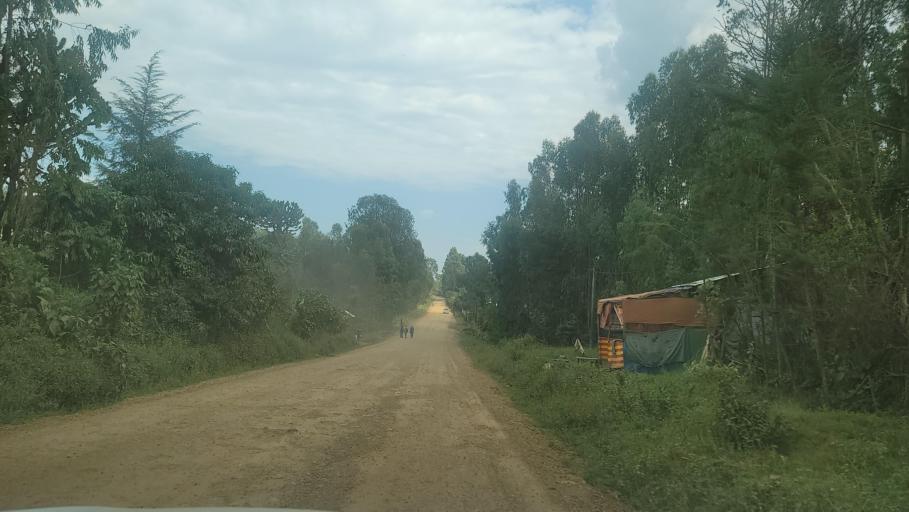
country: ET
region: Oromiya
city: Agaro
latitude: 7.7511
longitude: 36.2635
